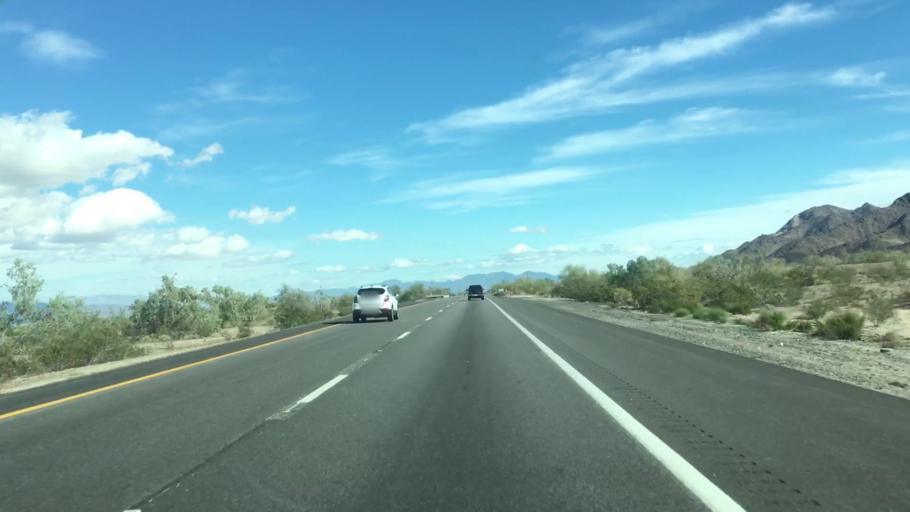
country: US
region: California
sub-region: Imperial County
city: Niland
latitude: 33.6861
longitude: -115.5249
